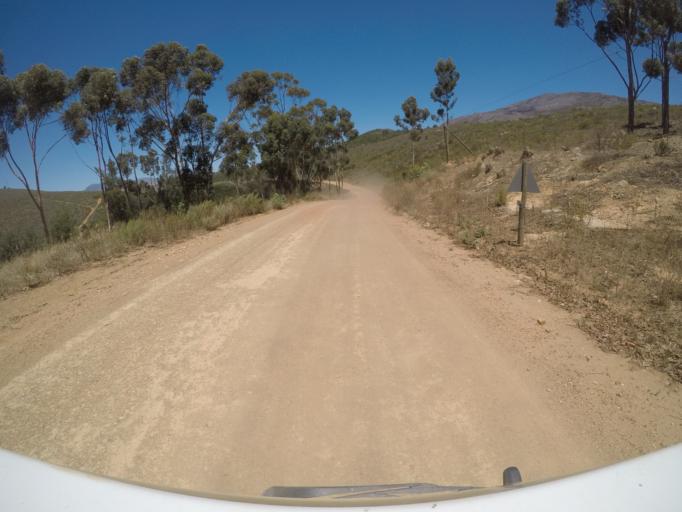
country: ZA
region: Western Cape
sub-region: Overberg District Municipality
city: Caledon
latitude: -34.1813
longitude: 19.2234
